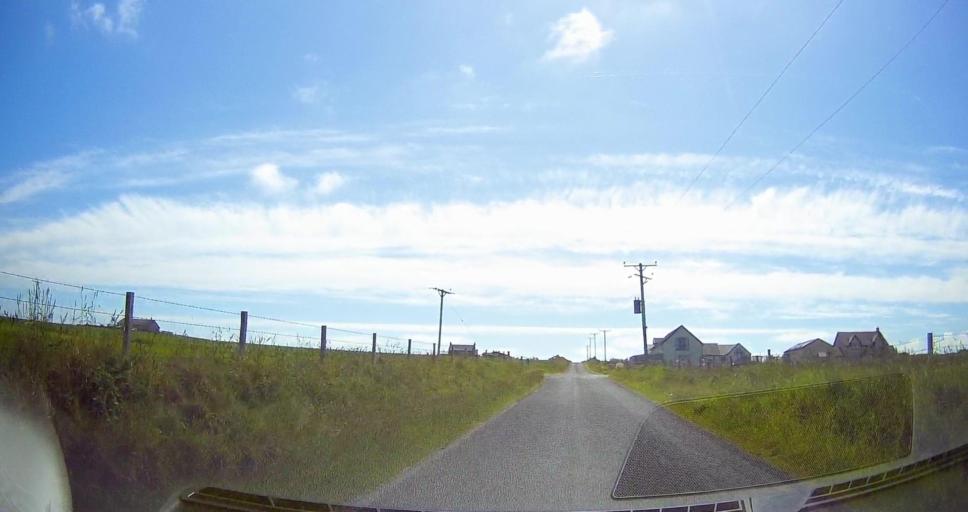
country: GB
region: Scotland
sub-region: Orkney Islands
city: Kirkwall
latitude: 58.8353
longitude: -2.9184
